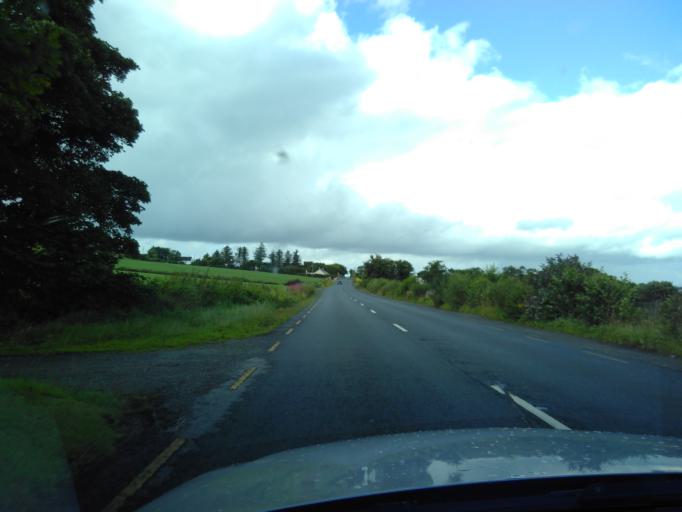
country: IE
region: Ulster
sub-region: County Donegal
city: Ramelton
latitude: 54.9961
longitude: -7.6625
